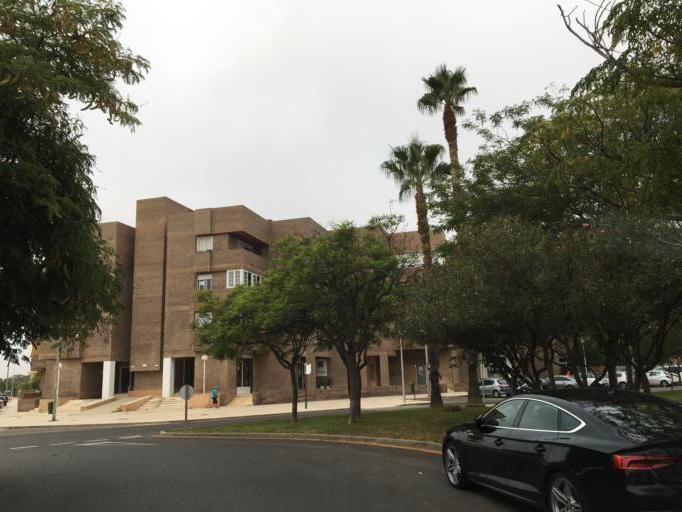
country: ES
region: Murcia
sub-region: Murcia
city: Cartagena
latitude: 37.6521
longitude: -1.0148
